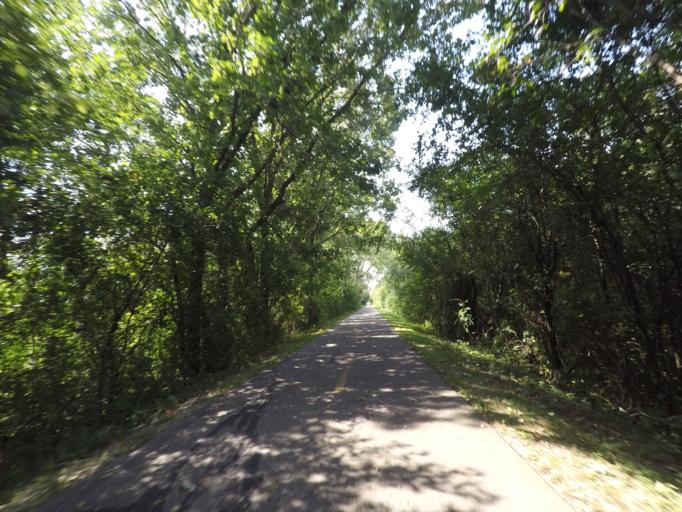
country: US
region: Wisconsin
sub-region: Jefferson County
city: Fort Atkinson
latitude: 42.8966
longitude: -88.8644
